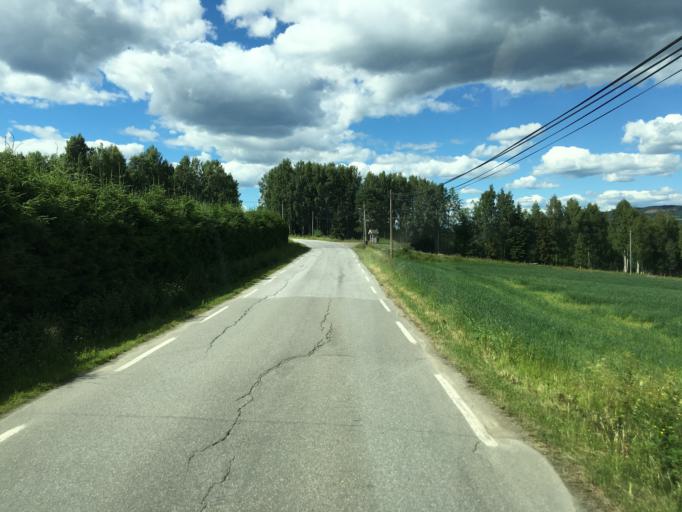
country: NO
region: Oppland
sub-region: Sondre Land
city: Hov
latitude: 60.6873
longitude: 10.3036
